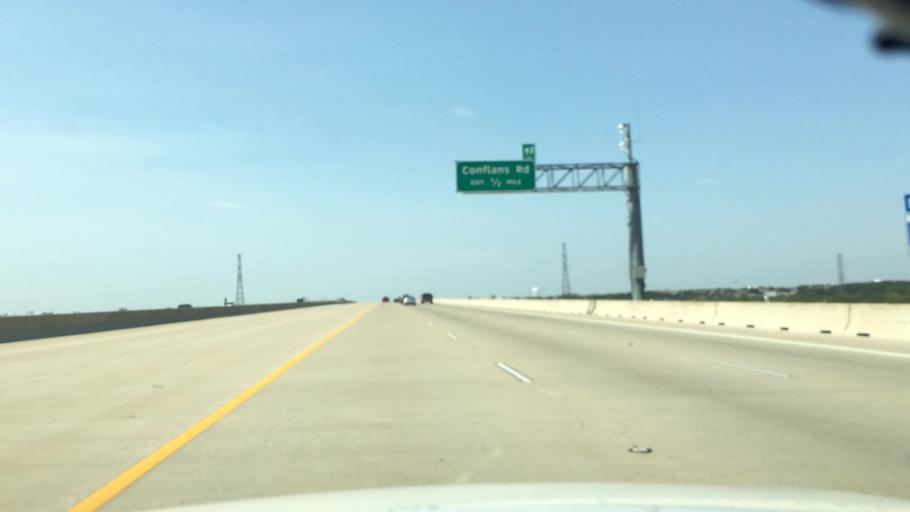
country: US
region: Texas
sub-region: Tarrant County
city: Euless
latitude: 32.8127
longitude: -97.0181
